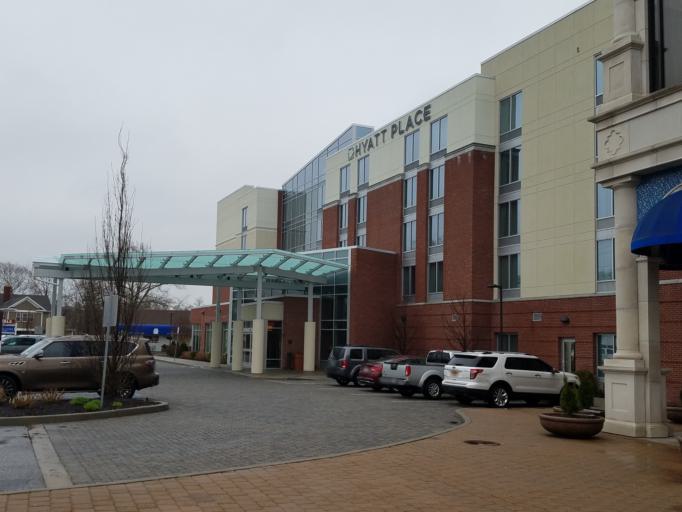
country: US
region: New York
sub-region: Suffolk County
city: Riverhead
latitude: 40.9183
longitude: -72.6573
